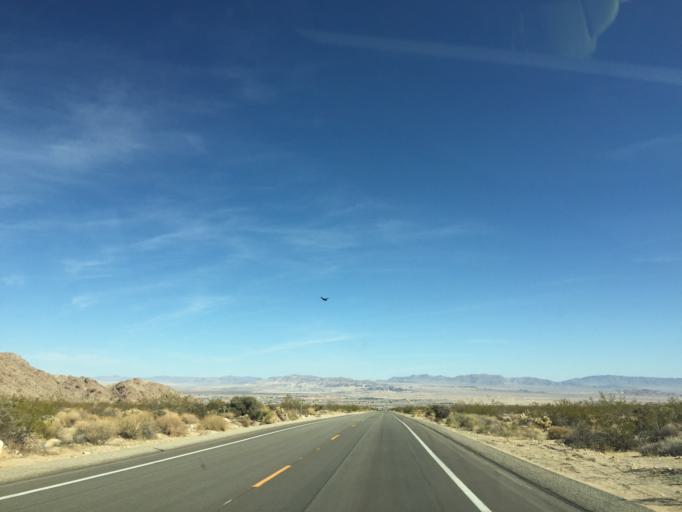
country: US
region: California
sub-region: San Bernardino County
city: Twentynine Palms
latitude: 34.0814
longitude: -116.0366
